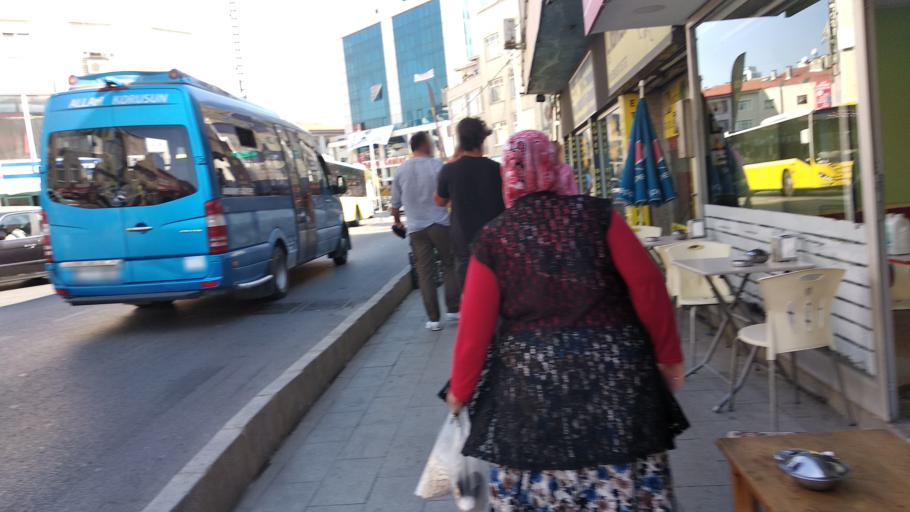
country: TR
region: Istanbul
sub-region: Atasehir
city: Atasehir
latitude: 40.9960
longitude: 29.0865
